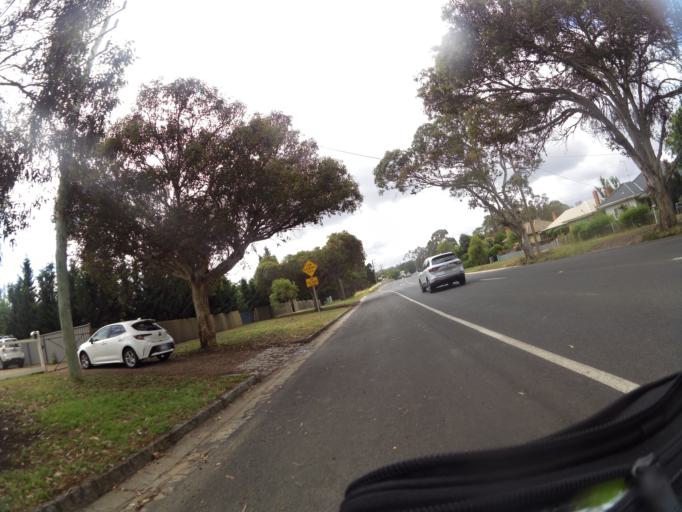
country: AU
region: Victoria
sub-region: Mount Alexander
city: Castlemaine
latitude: -37.0702
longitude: 144.2010
